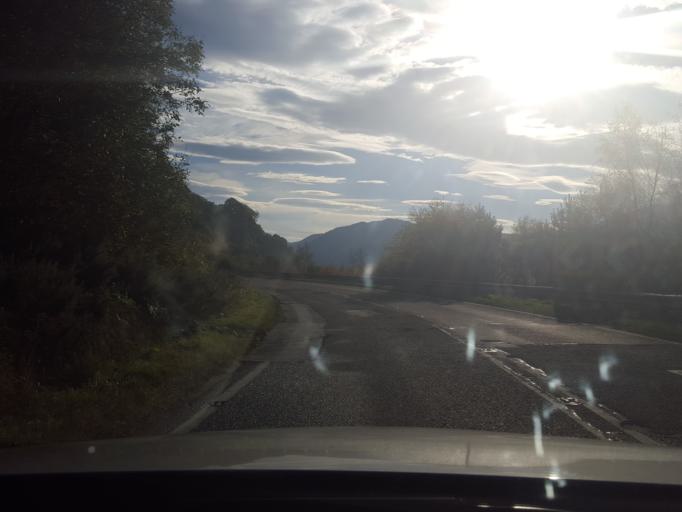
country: GB
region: Scotland
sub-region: Highland
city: Fort William
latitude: 57.2726
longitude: -5.5122
